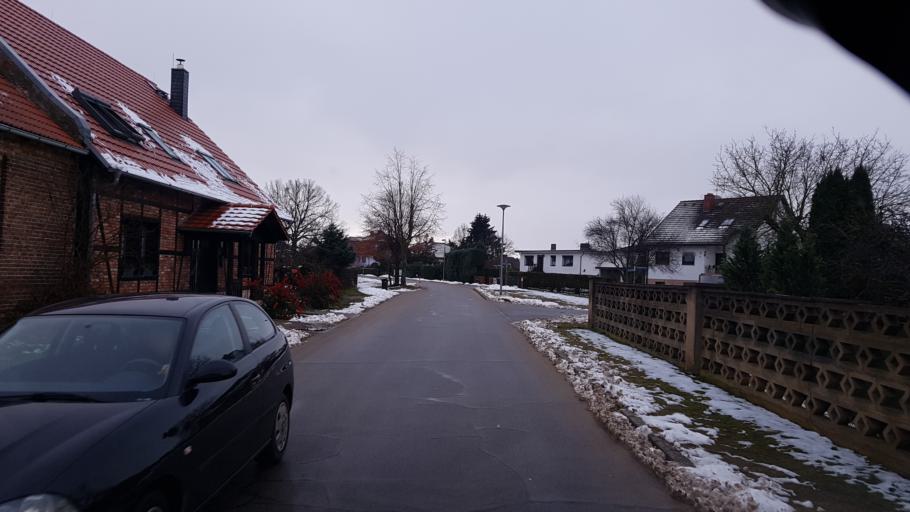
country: DE
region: Brandenburg
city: Luebben
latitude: 51.9403
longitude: 13.9122
